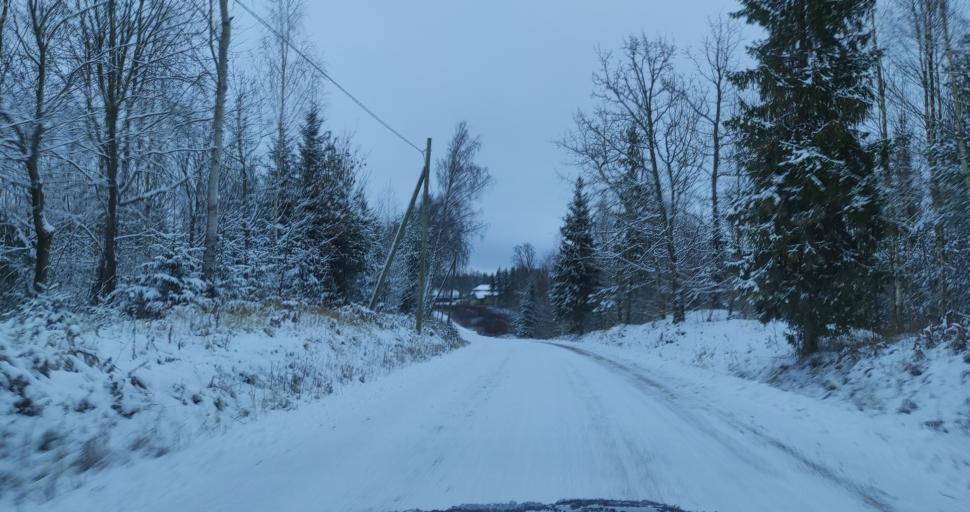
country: LV
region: Kuldigas Rajons
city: Kuldiga
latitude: 56.9496
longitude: 21.7779
